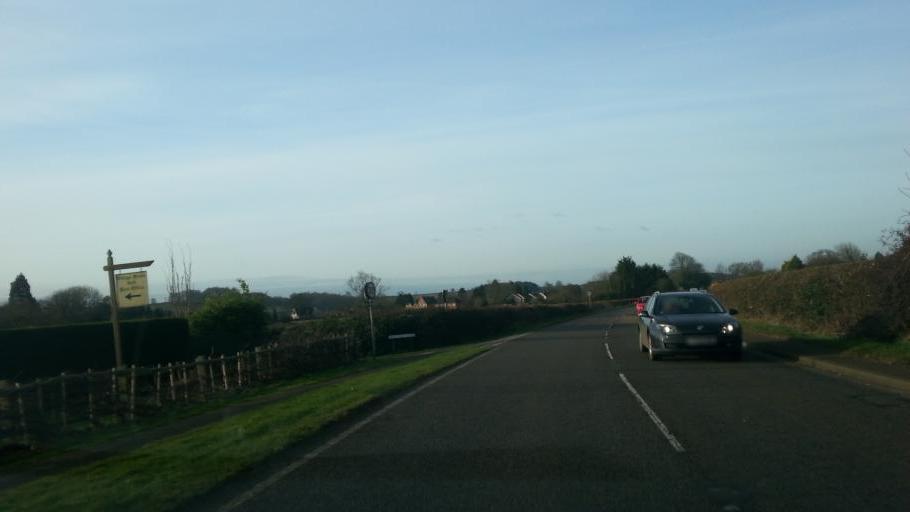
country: GB
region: England
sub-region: Lincolnshire
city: Barrowby
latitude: 52.8865
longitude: -0.6899
